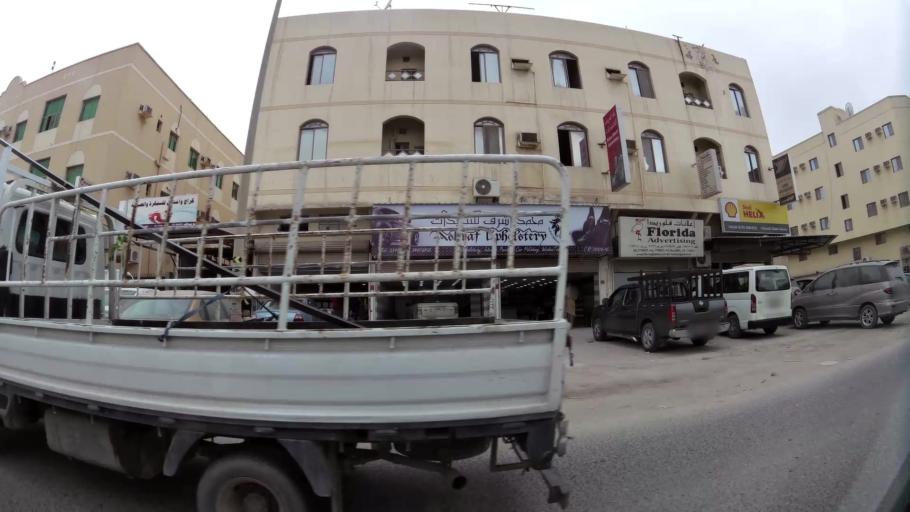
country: BH
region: Northern
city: Madinat `Isa
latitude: 26.1760
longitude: 50.5287
